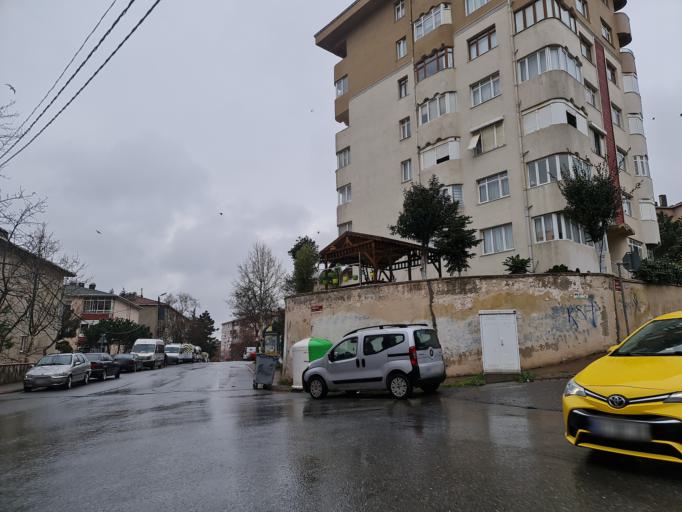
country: TR
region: Istanbul
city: Umraniye
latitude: 41.0130
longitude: 29.1046
